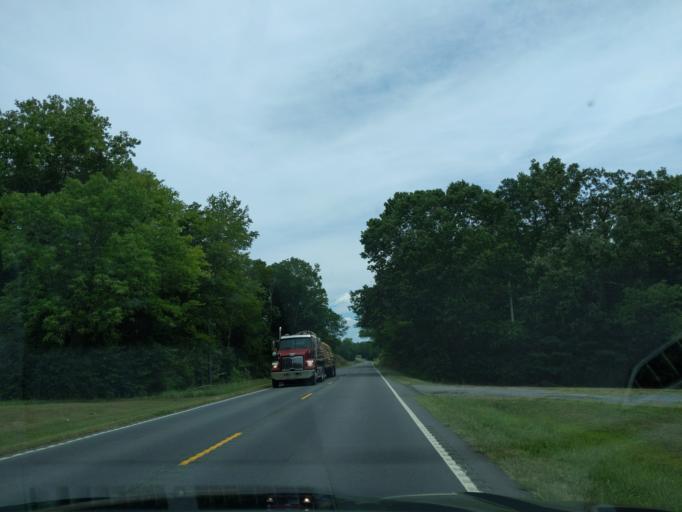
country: US
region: North Carolina
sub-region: Cabarrus County
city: Mount Pleasant
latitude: 35.4384
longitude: -80.3757
